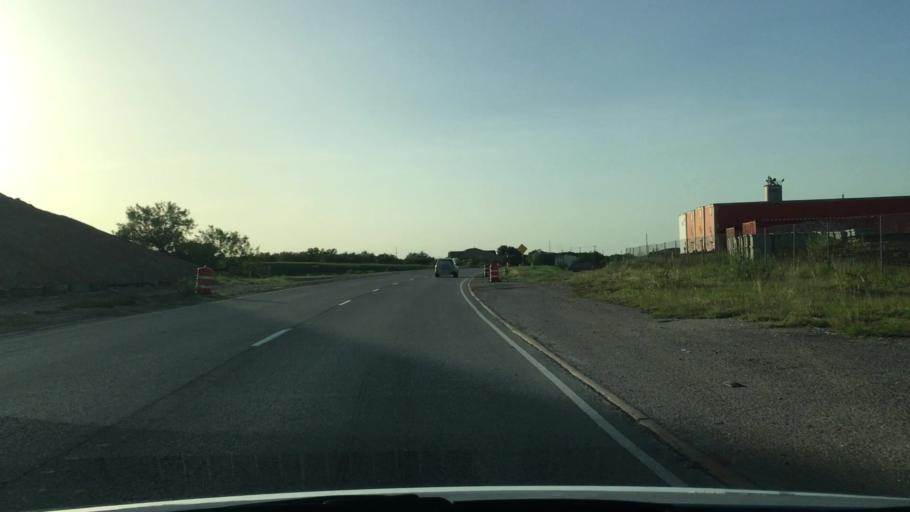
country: US
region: Texas
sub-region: Travis County
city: Austin
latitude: 30.2253
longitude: -97.6811
